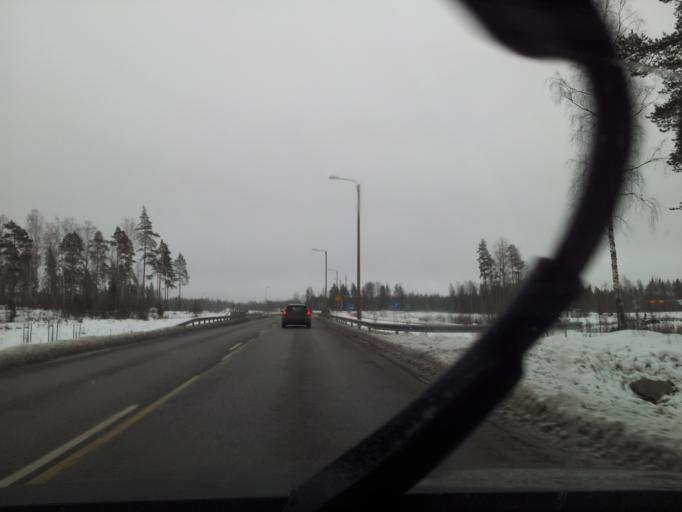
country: FI
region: Uusimaa
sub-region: Helsinki
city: Espoo
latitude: 60.1485
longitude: 24.5701
